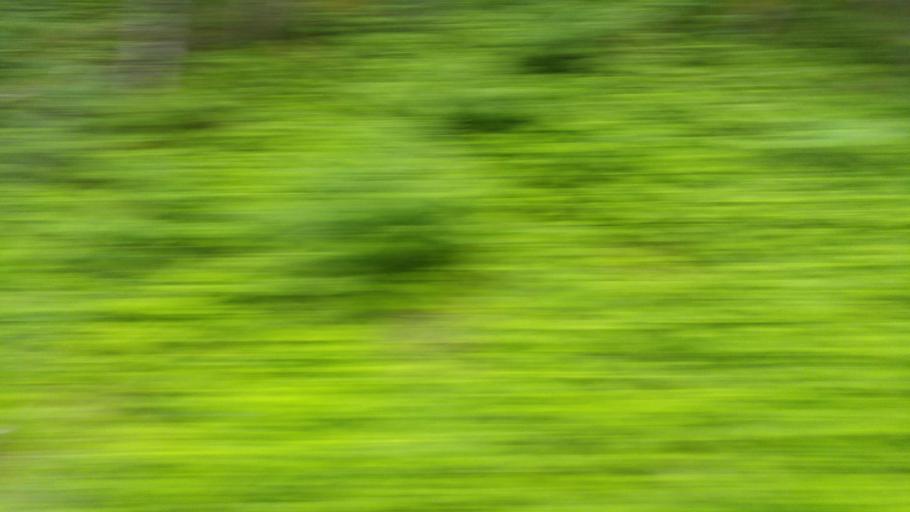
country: NO
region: Nord-Trondelag
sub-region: Meraker
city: Meraker
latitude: 63.4633
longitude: 11.5039
